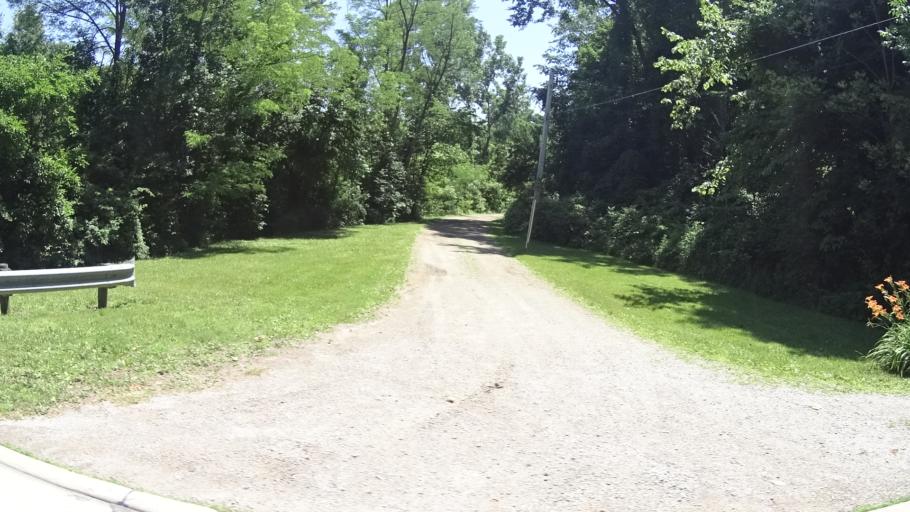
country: US
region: Ohio
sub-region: Lorain County
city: Vermilion
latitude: 41.3544
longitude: -82.4018
